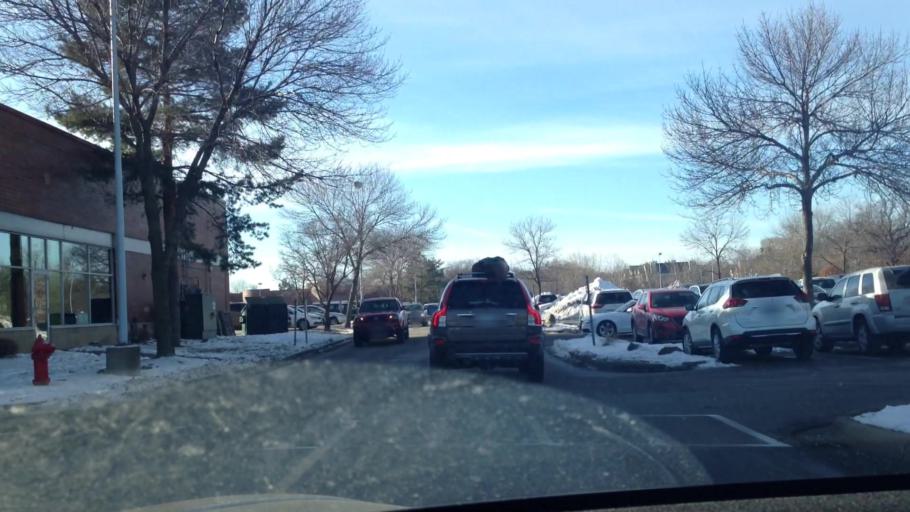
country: US
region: Minnesota
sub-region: Hennepin County
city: Minnetonka Mills
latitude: 44.9725
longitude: -93.4224
